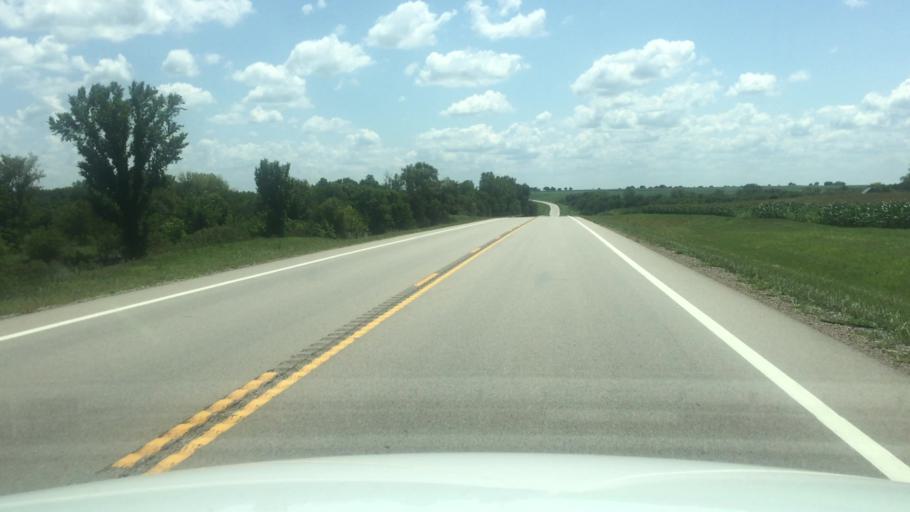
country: US
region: Kansas
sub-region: Brown County
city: Horton
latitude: 39.6284
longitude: -95.3512
